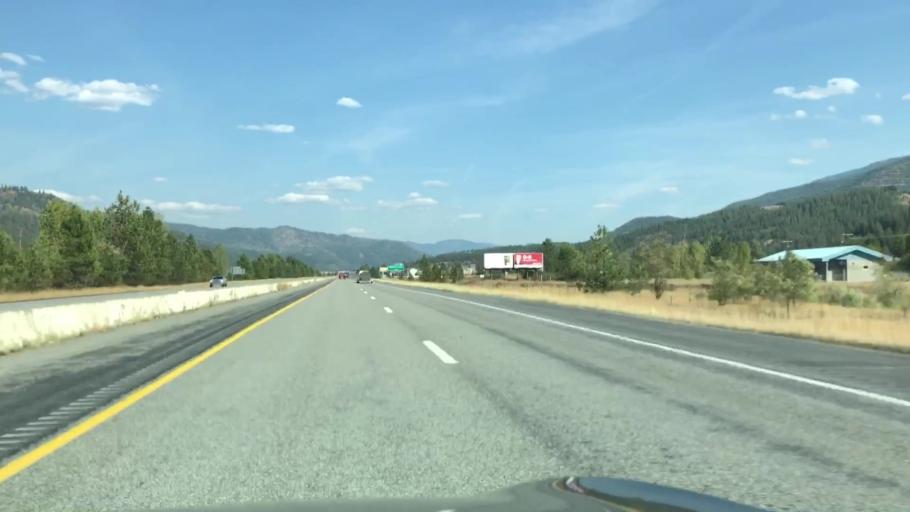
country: US
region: Idaho
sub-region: Shoshone County
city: Pinehurst
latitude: 47.5461
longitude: -116.2056
